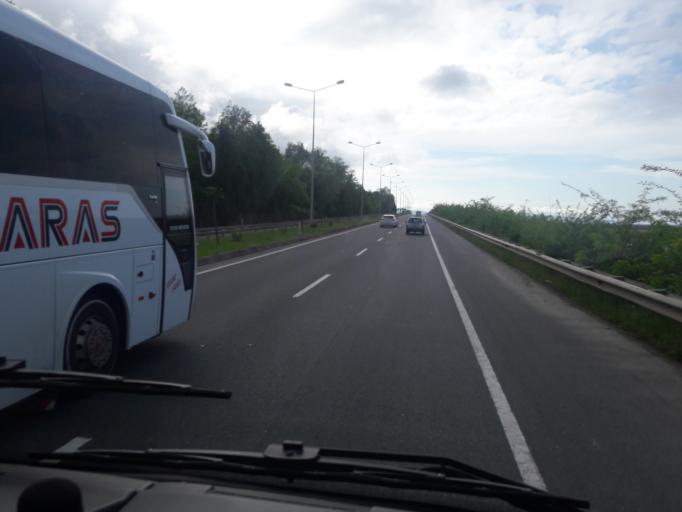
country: TR
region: Giresun
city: Piraziz
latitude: 40.9616
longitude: 38.1024
